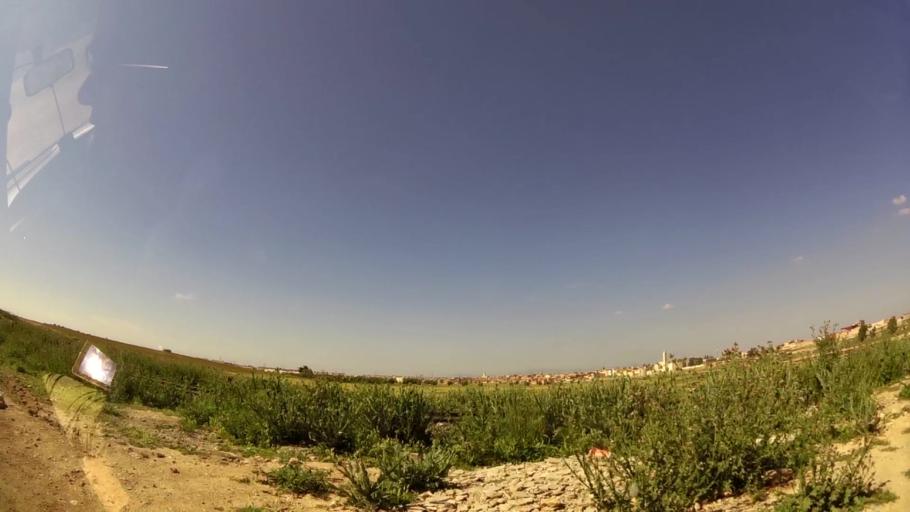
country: MA
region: Oriental
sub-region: Oujda-Angad
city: Oujda
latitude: 34.6918
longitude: -1.9272
